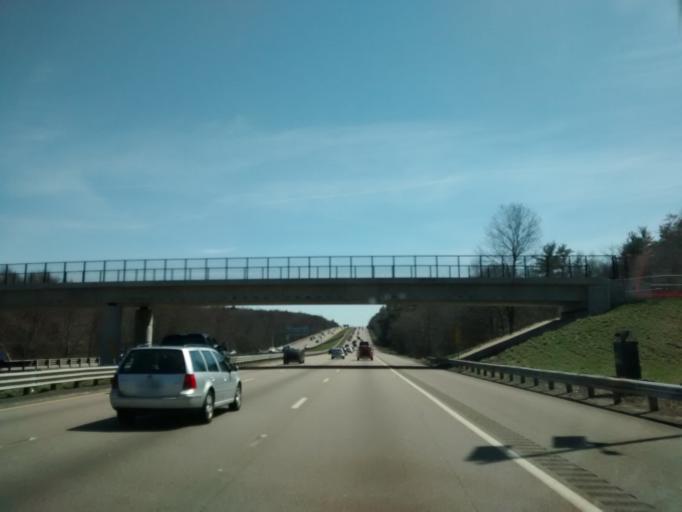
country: US
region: Massachusetts
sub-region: Norfolk County
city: Randolph
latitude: 42.1936
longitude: -71.0781
